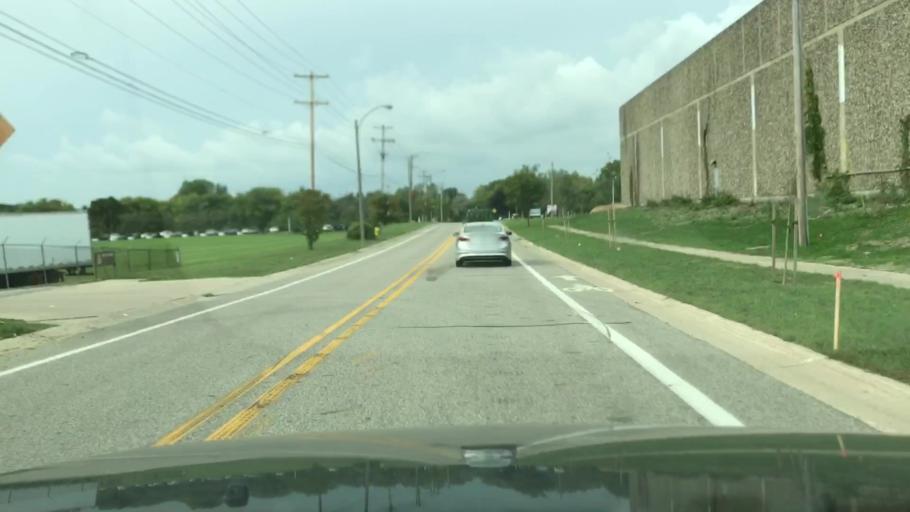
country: US
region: Michigan
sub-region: Kent County
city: East Grand Rapids
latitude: 42.9721
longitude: -85.6005
